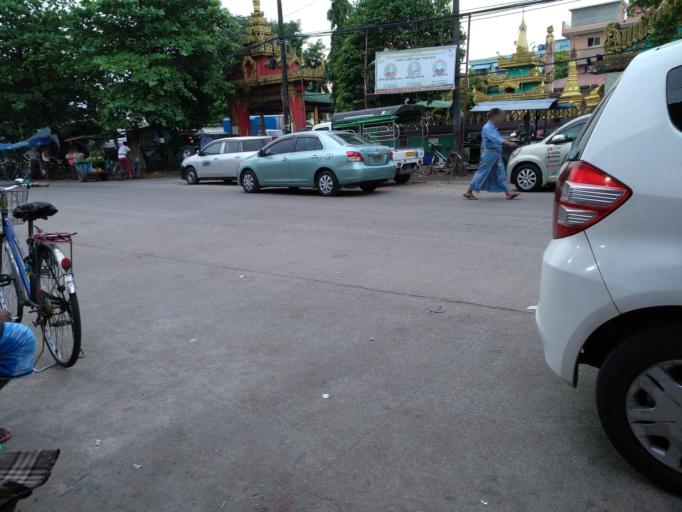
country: MM
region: Yangon
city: Yangon
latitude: 16.8372
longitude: 96.1177
